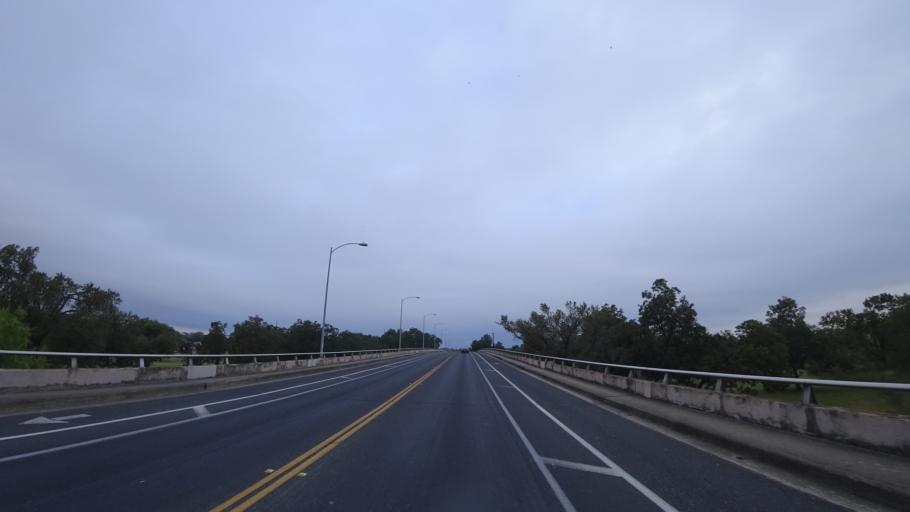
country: US
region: Texas
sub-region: Travis County
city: Austin
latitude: 30.2695
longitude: -97.7120
